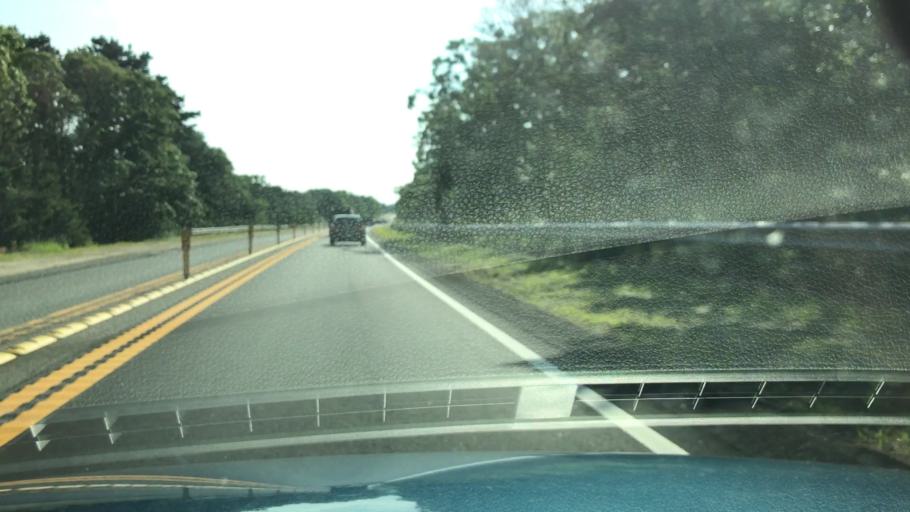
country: US
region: Massachusetts
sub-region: Barnstable County
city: Harwich Center
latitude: 41.7141
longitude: -70.0619
